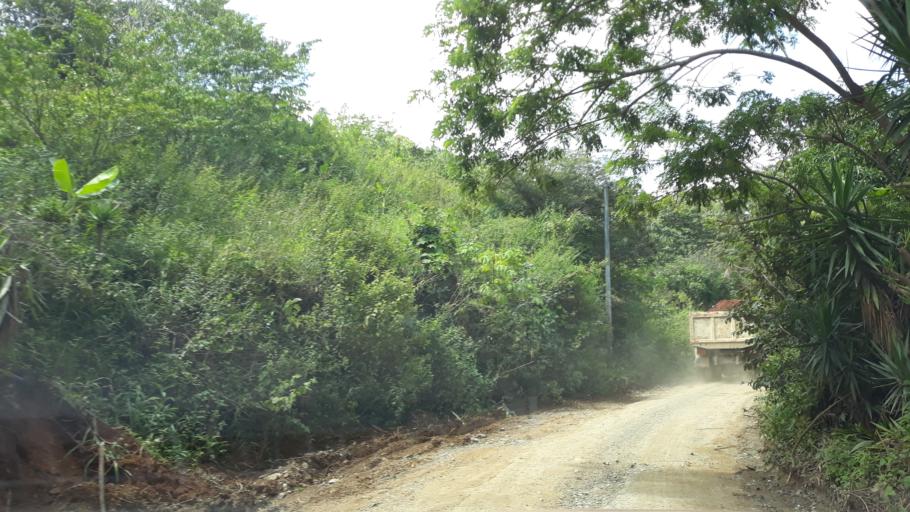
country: HN
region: El Paraiso
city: Santa Cruz
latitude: 13.7545
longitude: -86.6566
